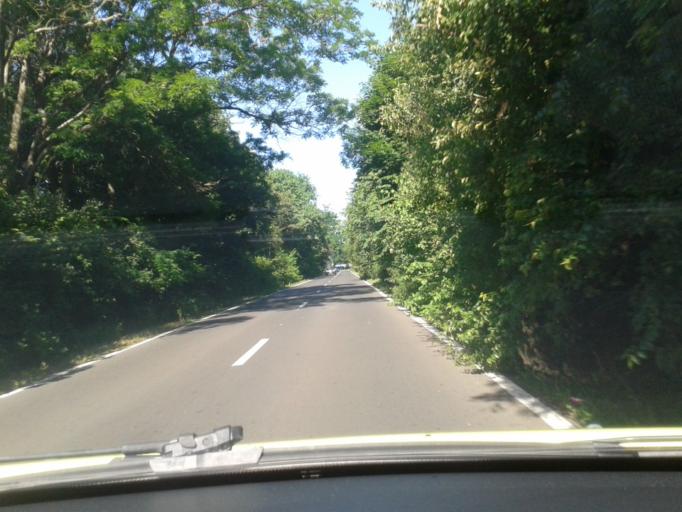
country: RO
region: Constanta
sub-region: Comuna Douazeci si Trei August
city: Dulcesti
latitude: 43.8749
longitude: 28.5774
